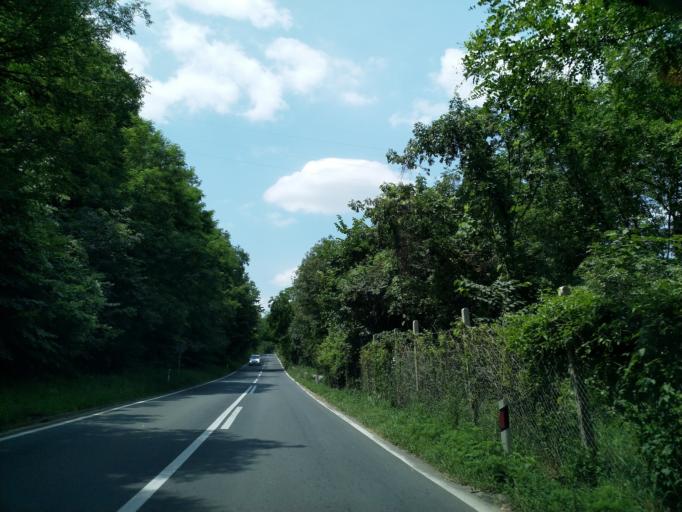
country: RS
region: Central Serbia
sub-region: Rasinski Okrug
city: Aleksandrovac
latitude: 43.4178
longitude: 21.1893
